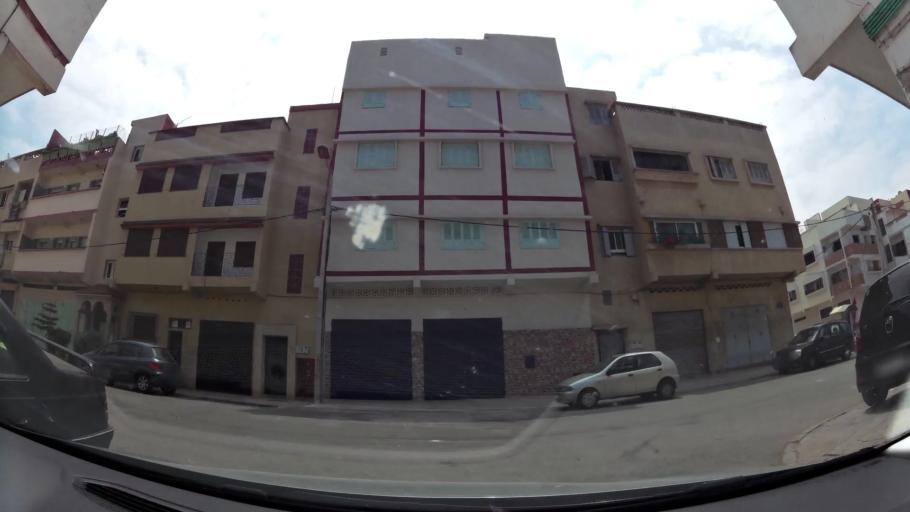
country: MA
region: Rabat-Sale-Zemmour-Zaer
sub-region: Rabat
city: Rabat
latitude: 33.9884
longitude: -6.8824
